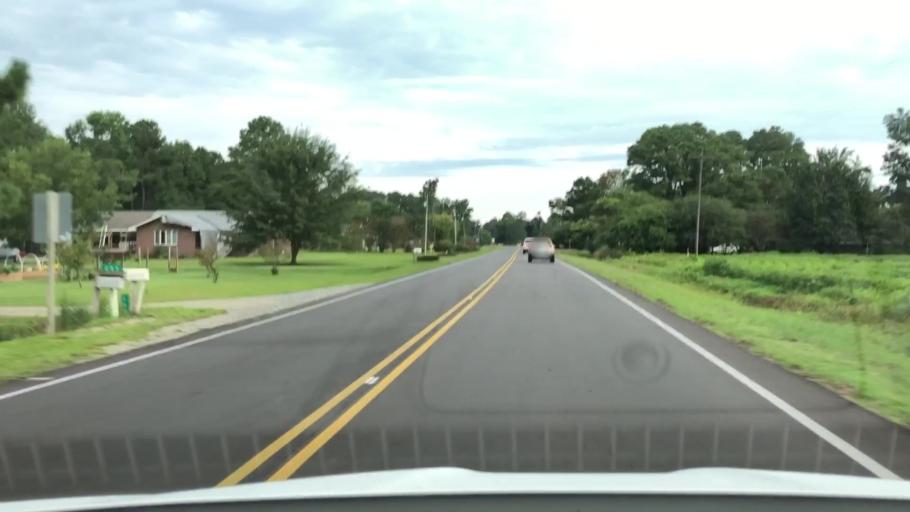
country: US
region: North Carolina
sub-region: Jones County
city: Maysville
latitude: 34.8976
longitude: -77.2209
